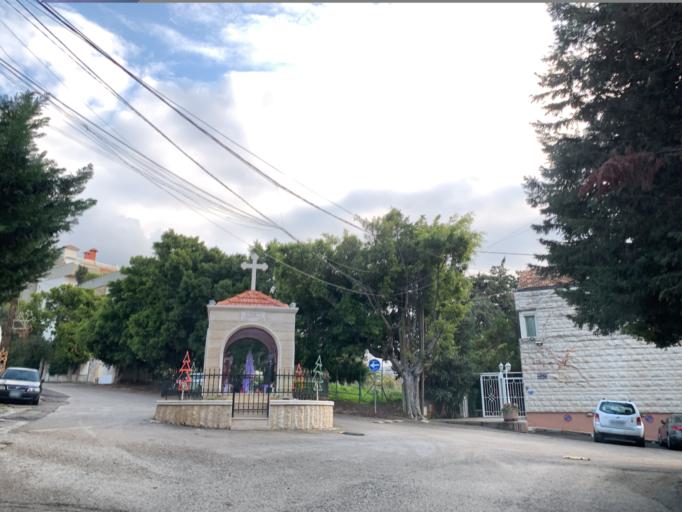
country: LB
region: Mont-Liban
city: Baabda
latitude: 33.8521
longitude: 35.5782
